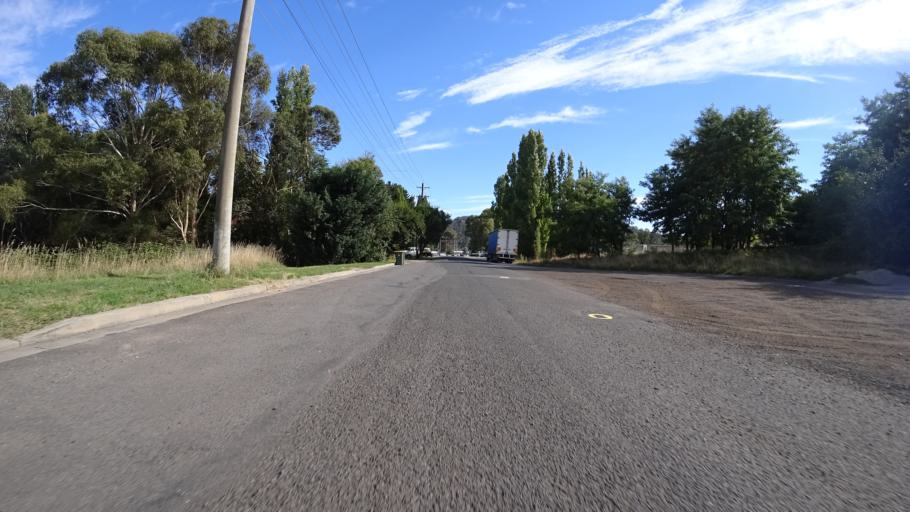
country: AU
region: New South Wales
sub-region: Lithgow
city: Lithgow
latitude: -33.4789
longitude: 150.1748
